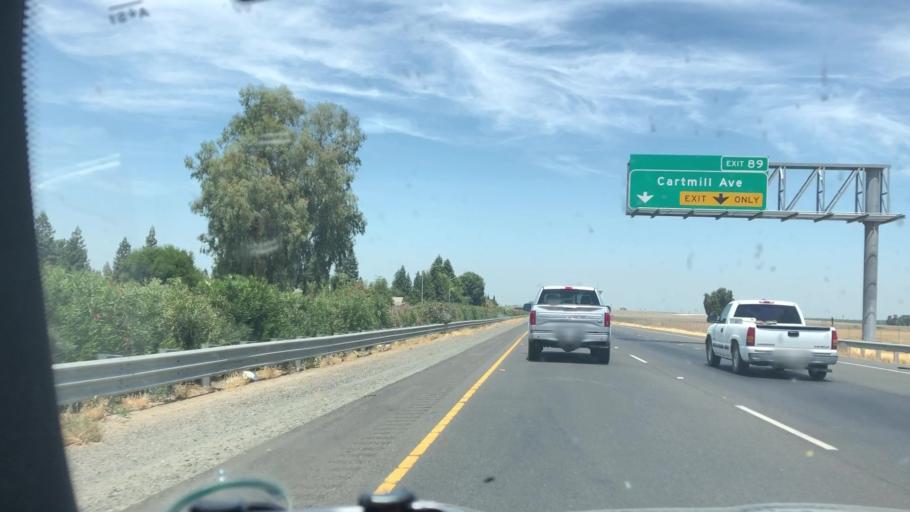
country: US
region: California
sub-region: Tulare County
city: Tulare
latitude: 36.2322
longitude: -119.3397
